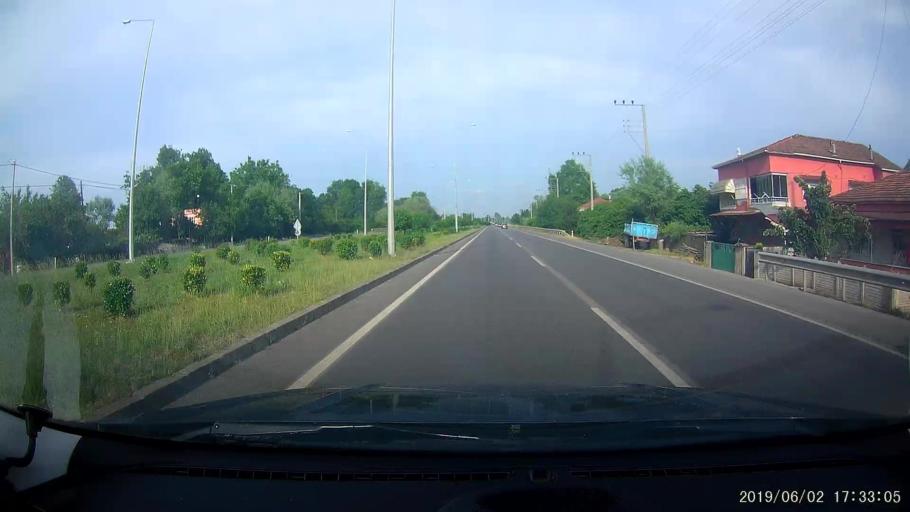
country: TR
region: Samsun
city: Carsamba
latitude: 41.2207
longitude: 36.8409
